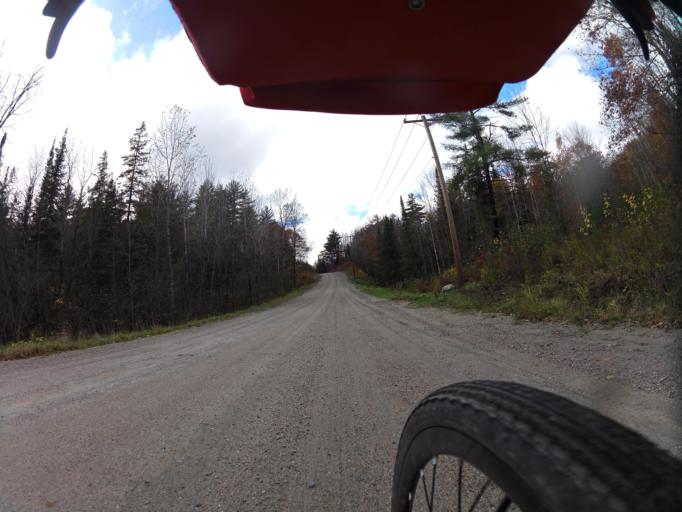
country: CA
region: Quebec
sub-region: Outaouais
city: Wakefield
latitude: 45.6971
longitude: -76.0416
